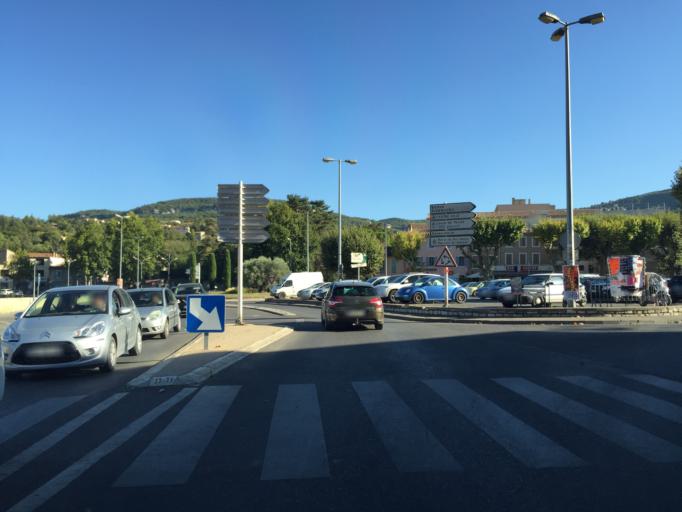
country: FR
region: Provence-Alpes-Cote d'Azur
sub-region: Departement du Vaucluse
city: Apt
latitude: 43.8758
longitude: 5.4002
